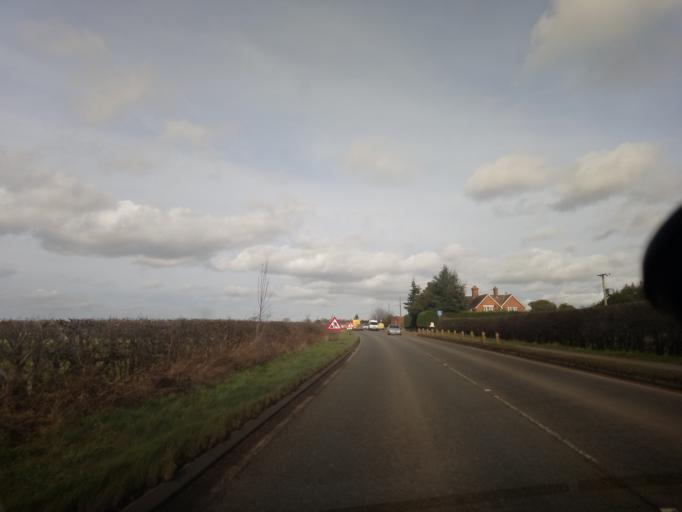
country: GB
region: England
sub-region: Telford and Wrekin
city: Eyton upon the Weald Moors
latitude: 52.7627
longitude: -2.5469
